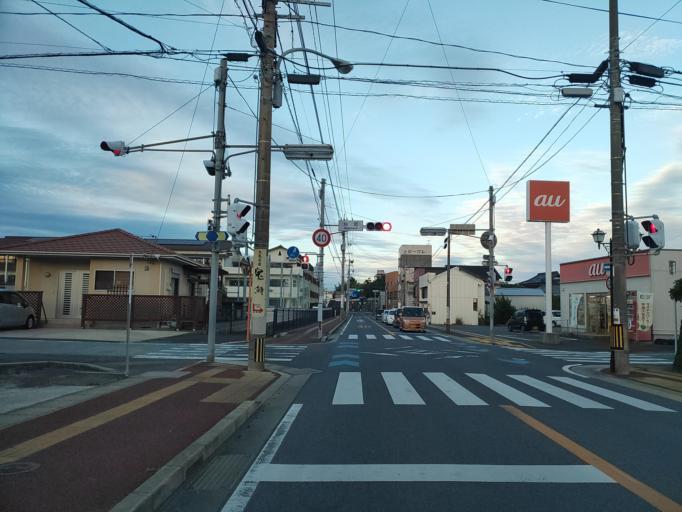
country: JP
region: Nagasaki
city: Fukuecho
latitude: 32.6916
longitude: 128.8425
